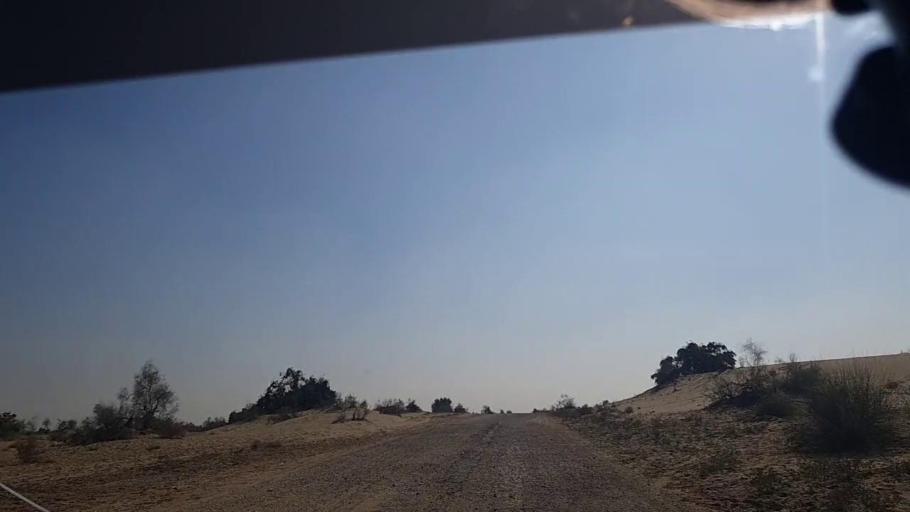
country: PK
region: Sindh
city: Khanpur
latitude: 27.5742
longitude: 69.3054
